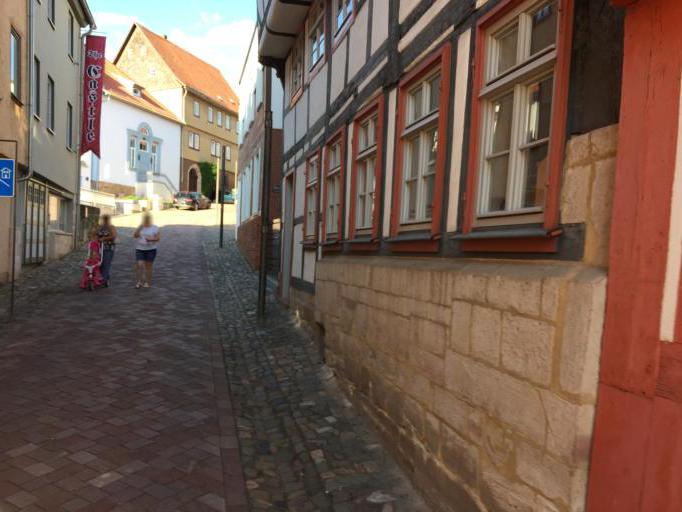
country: DE
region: Thuringia
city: Schmalkalden
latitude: 50.7226
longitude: 10.4532
